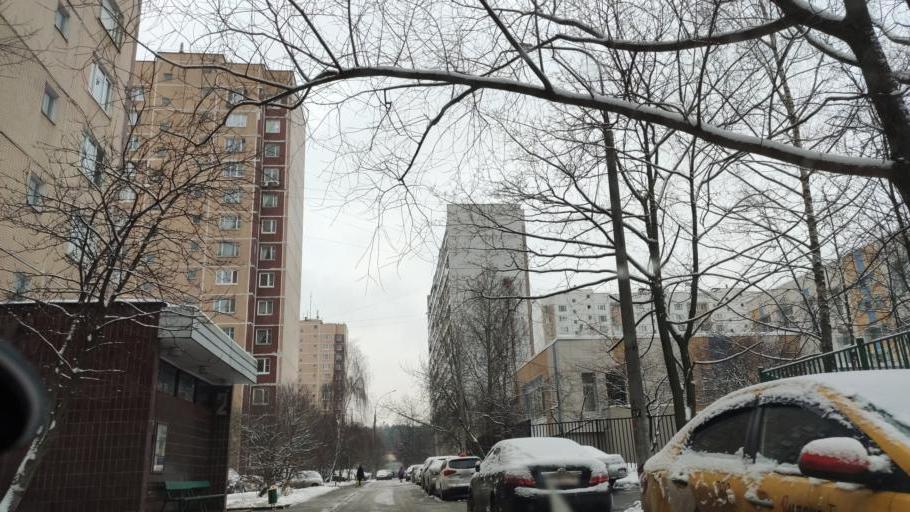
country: RU
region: Moscow
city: Solntsevo
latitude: 55.6373
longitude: 37.3611
